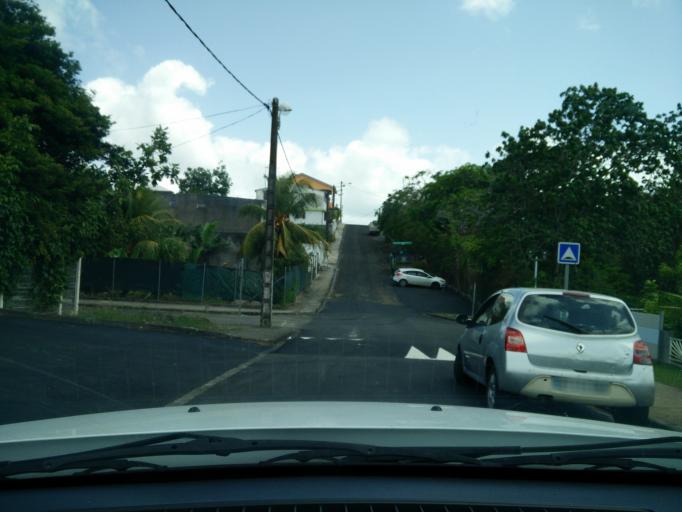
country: GP
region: Guadeloupe
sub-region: Guadeloupe
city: Petit-Canal
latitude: 16.3809
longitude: -61.4878
